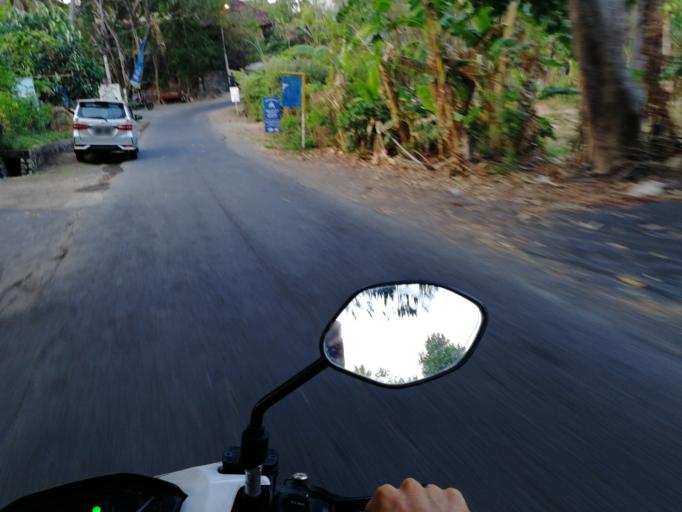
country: ID
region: Bali
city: Biaslantang Kaler
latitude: -8.3486
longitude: 115.6805
